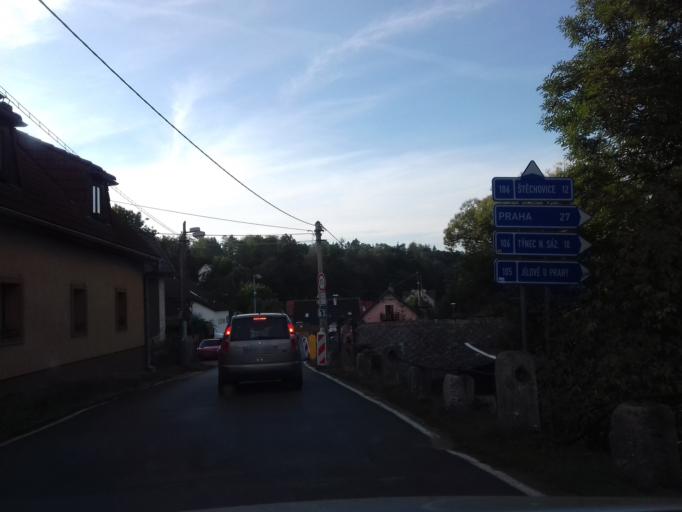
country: CZ
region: Central Bohemia
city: Kamenny Privoz
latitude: 49.8604
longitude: 14.5046
